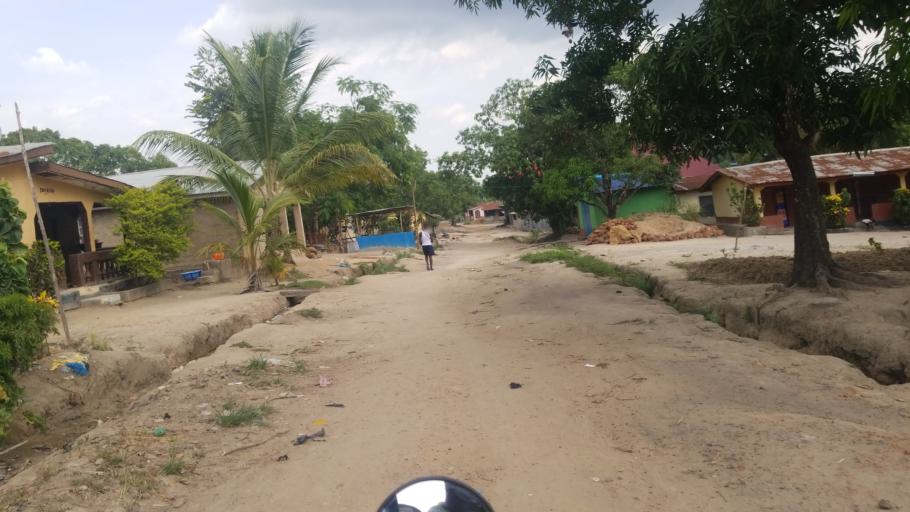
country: SL
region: Western Area
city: Waterloo
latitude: 8.3252
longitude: -13.0525
